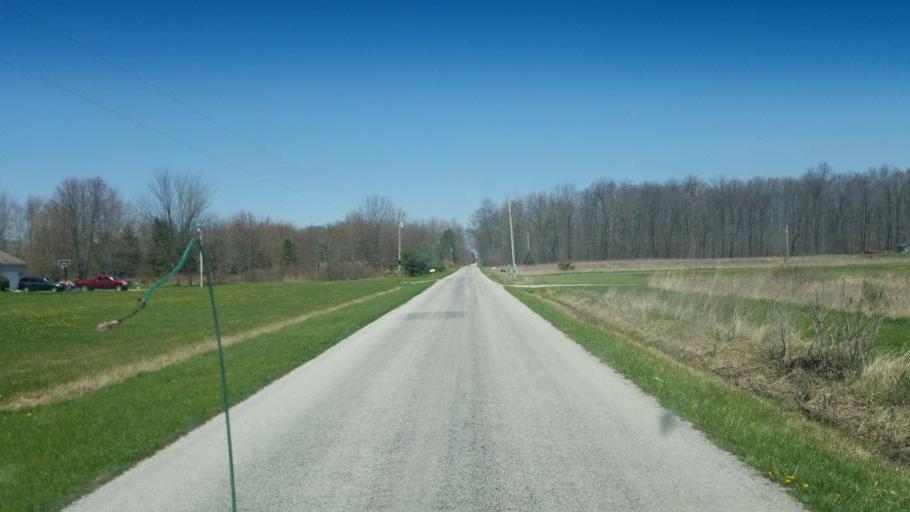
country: US
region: Ohio
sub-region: Huron County
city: New London
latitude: 41.0525
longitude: -82.4362
